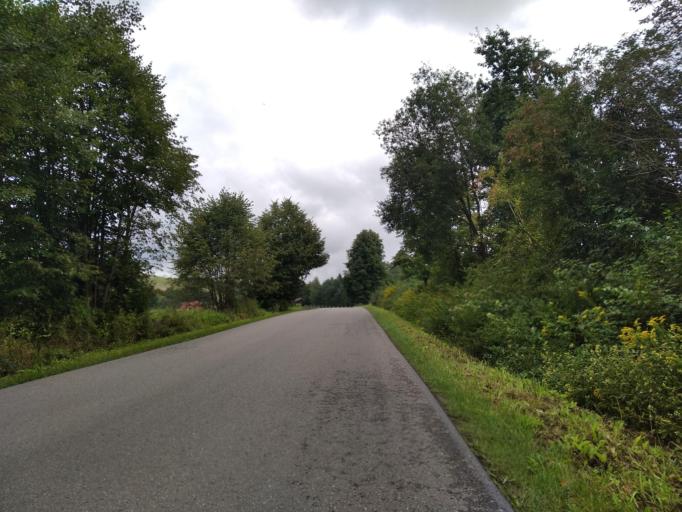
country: PL
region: Subcarpathian Voivodeship
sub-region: Powiat brzozowski
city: Nozdrzec
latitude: 49.7343
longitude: 22.2639
